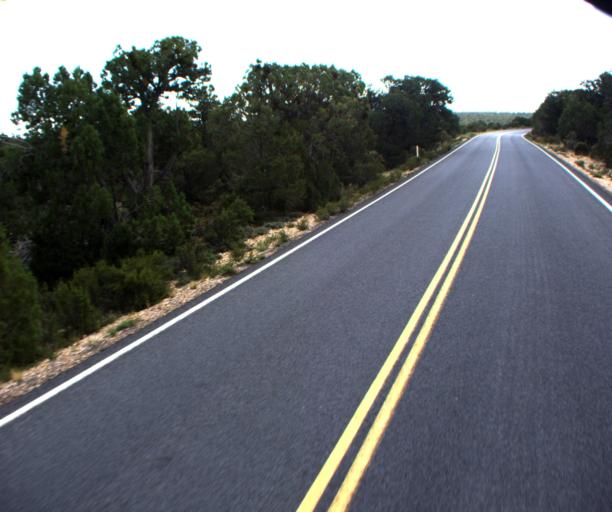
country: US
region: Arizona
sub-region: Coconino County
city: Grand Canyon
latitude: 36.0189
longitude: -111.8110
